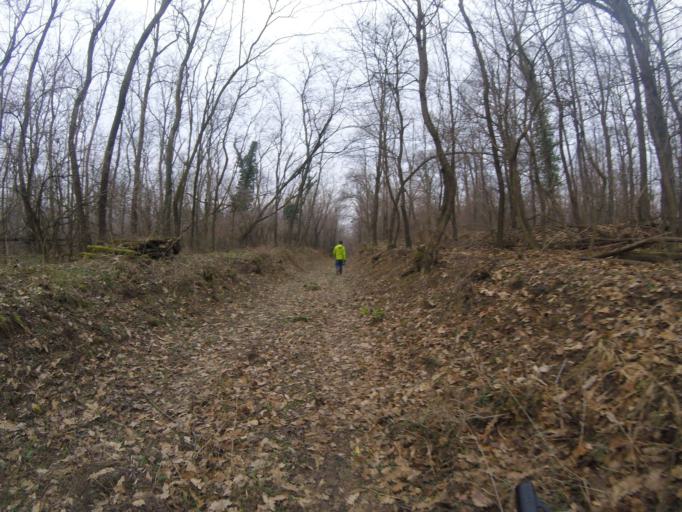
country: HU
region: Baranya
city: Pecsvarad
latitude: 46.1364
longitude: 18.5223
